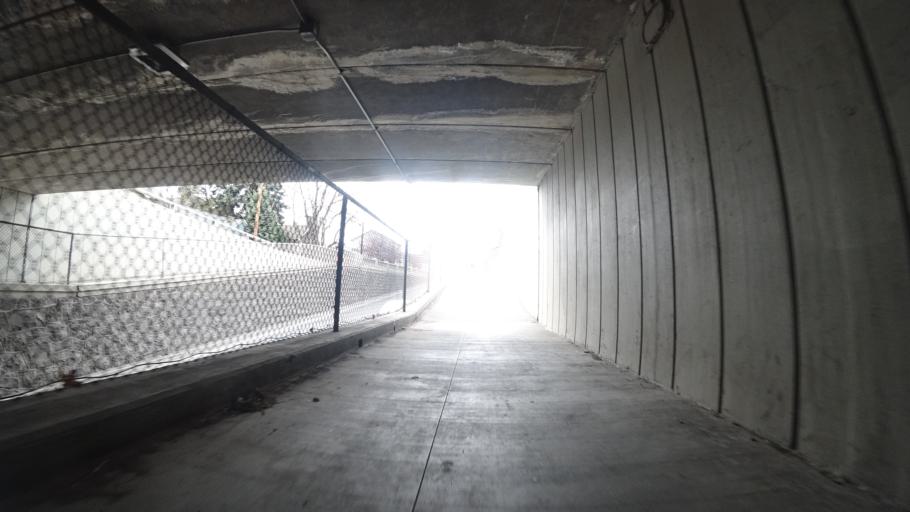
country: US
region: Oregon
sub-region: Deschutes County
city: Bend
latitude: 44.0560
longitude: -121.3072
